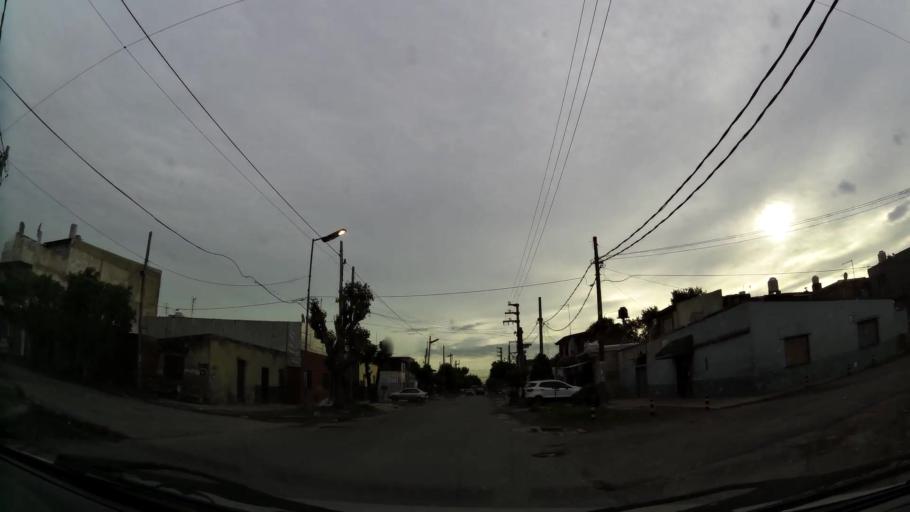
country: AR
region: Buenos Aires
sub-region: Partido de Lanus
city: Lanus
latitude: -34.7268
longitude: -58.3372
